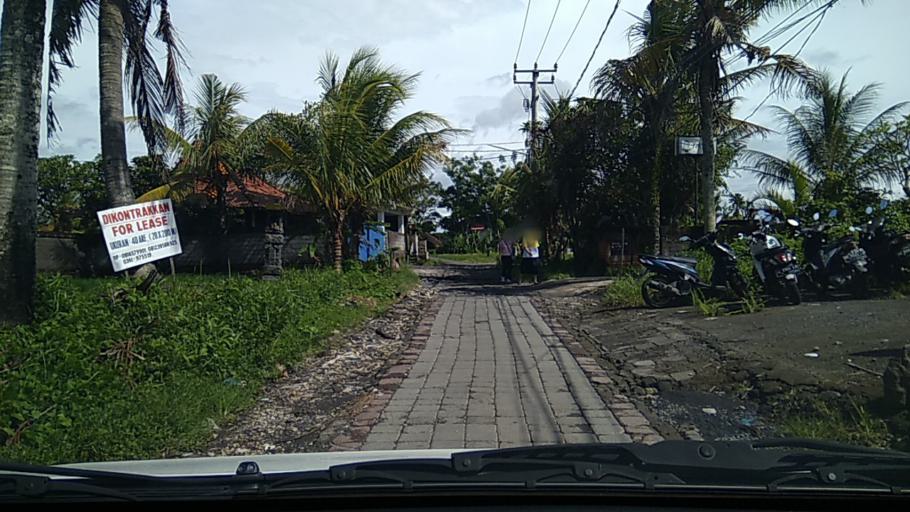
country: ID
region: Bali
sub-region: Kabupaten Gianyar
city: Ubud
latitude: -8.5144
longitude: 115.2582
